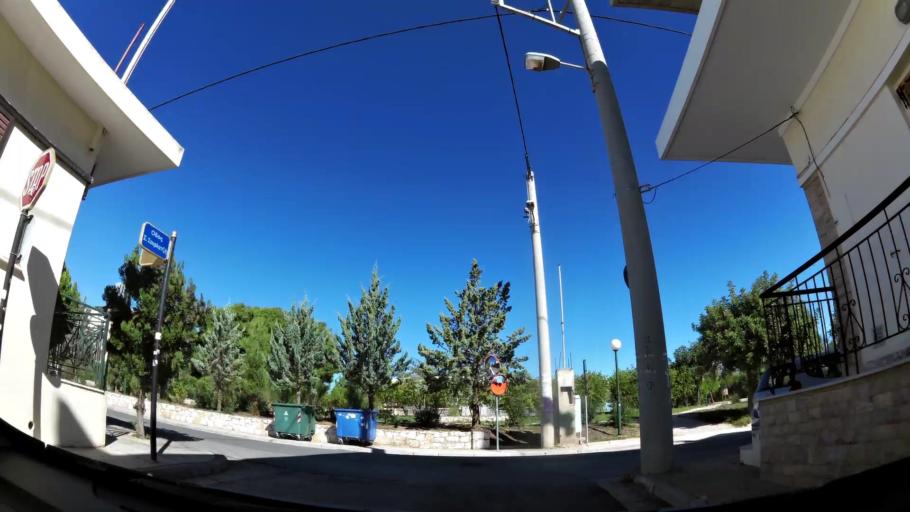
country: GR
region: Attica
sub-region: Nomarchia Anatolikis Attikis
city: Koropi
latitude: 37.9014
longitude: 23.8771
